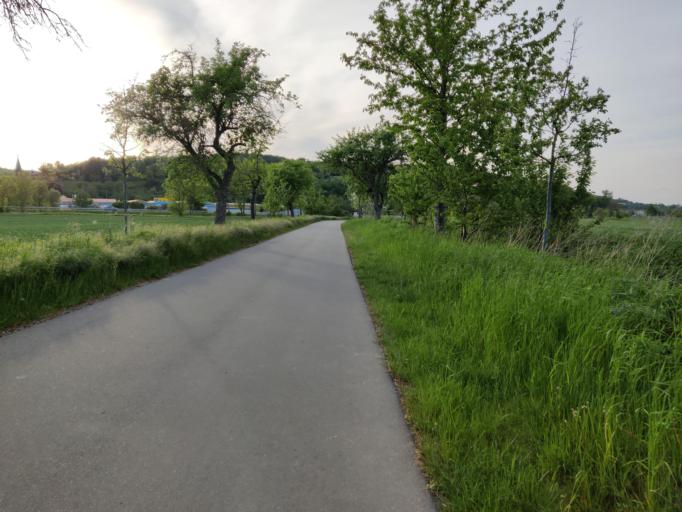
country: DE
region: Saxony-Anhalt
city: Naumburg
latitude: 51.1708
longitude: 11.7841
